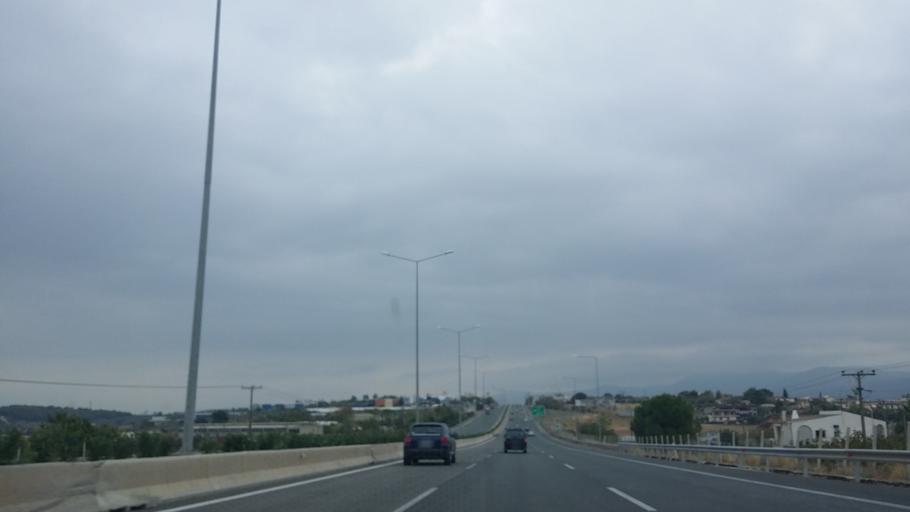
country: GR
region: Central Greece
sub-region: Nomos Voiotias
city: Schimatari
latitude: 38.3294
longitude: 23.6054
